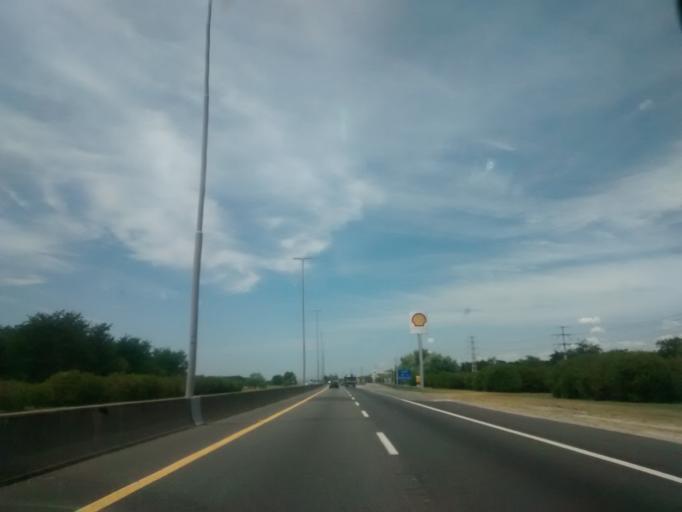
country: AR
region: Buenos Aires
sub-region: Partido de Quilmes
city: Quilmes
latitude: -34.8109
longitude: -58.1159
